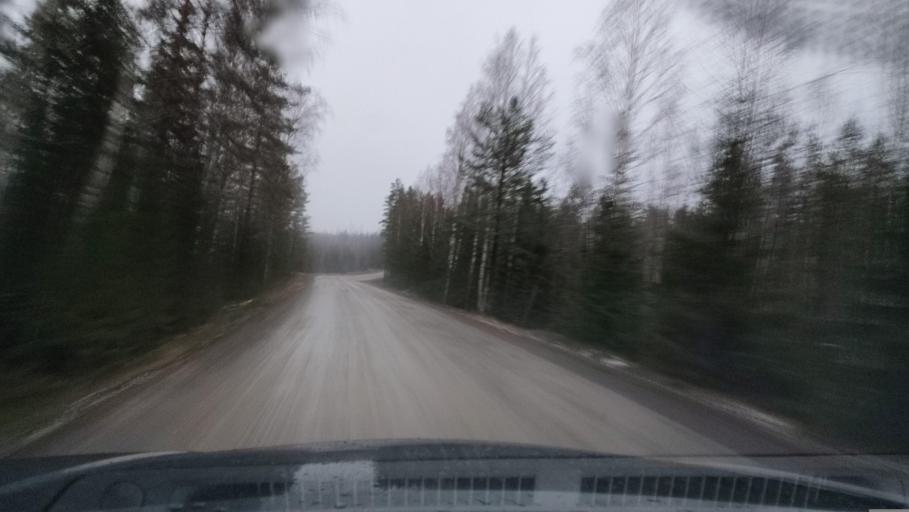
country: FI
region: Southern Ostrobothnia
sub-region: Suupohja
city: Karijoki
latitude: 62.1272
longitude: 21.6102
